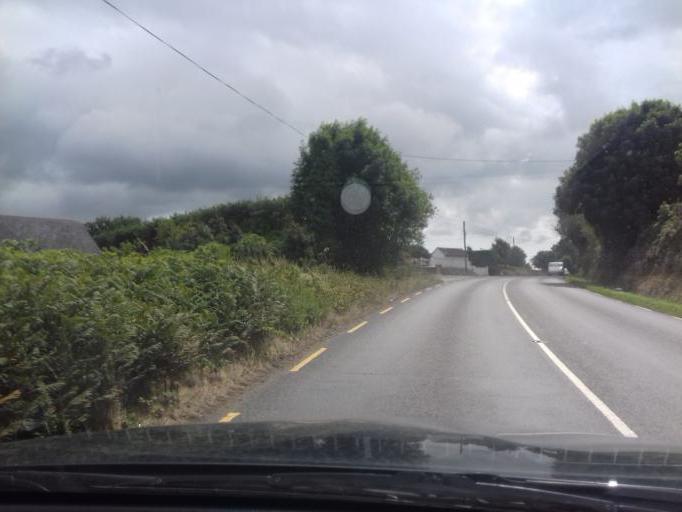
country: IE
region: Leinster
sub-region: Loch Garman
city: Ballinroad
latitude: 52.4581
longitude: -6.4001
